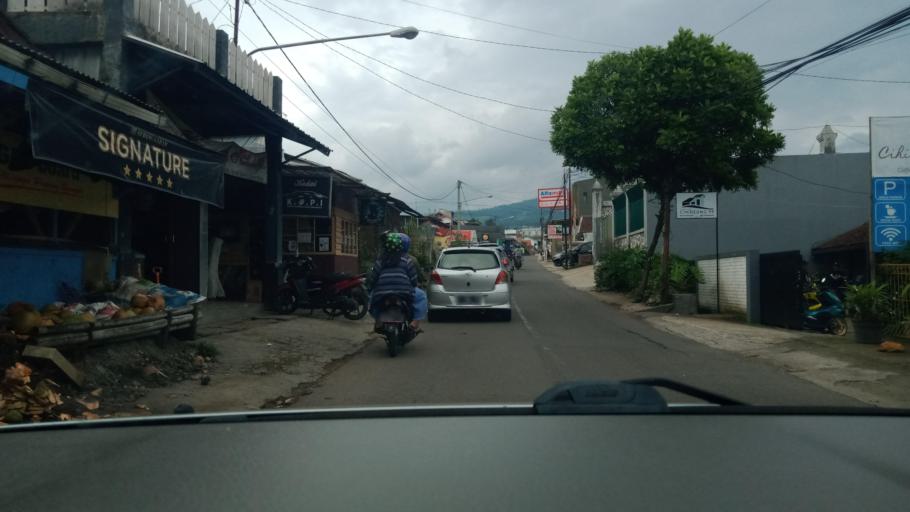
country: ID
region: West Java
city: Lembang
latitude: -6.8180
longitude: 107.5947
